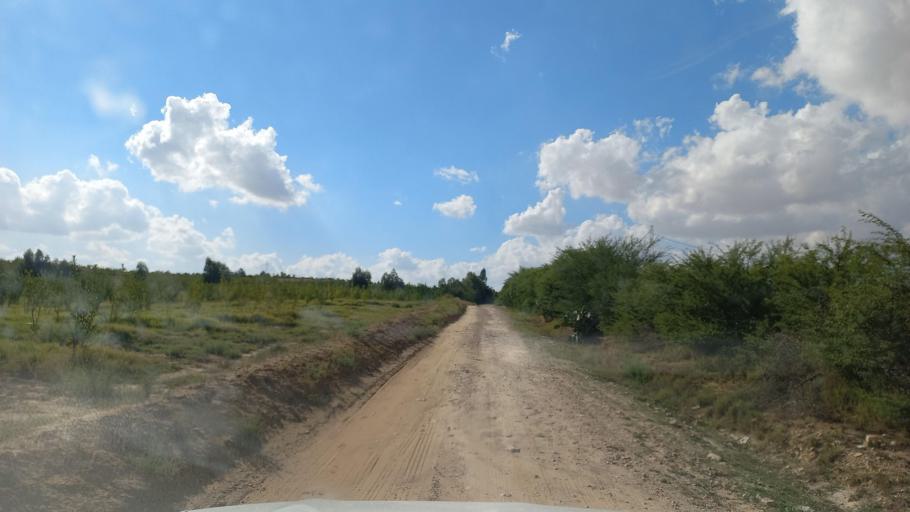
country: TN
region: Al Qasrayn
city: Sbiba
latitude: 35.3356
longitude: 9.0839
